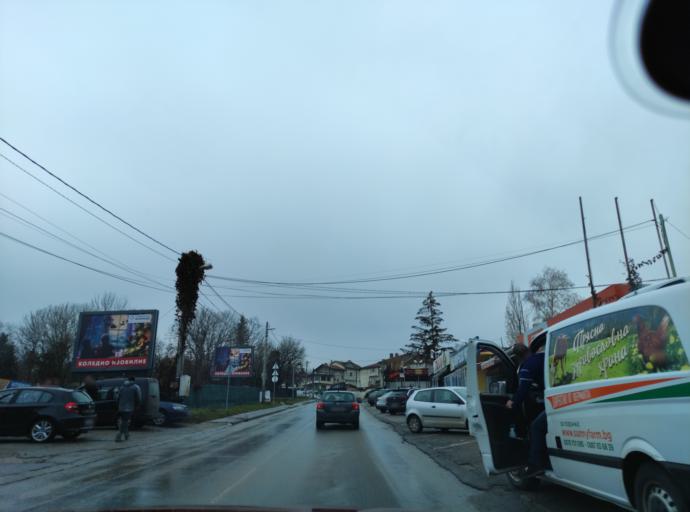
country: BG
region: Sofia-Capital
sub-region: Stolichna Obshtina
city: Sofia
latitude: 42.6358
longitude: 23.3106
